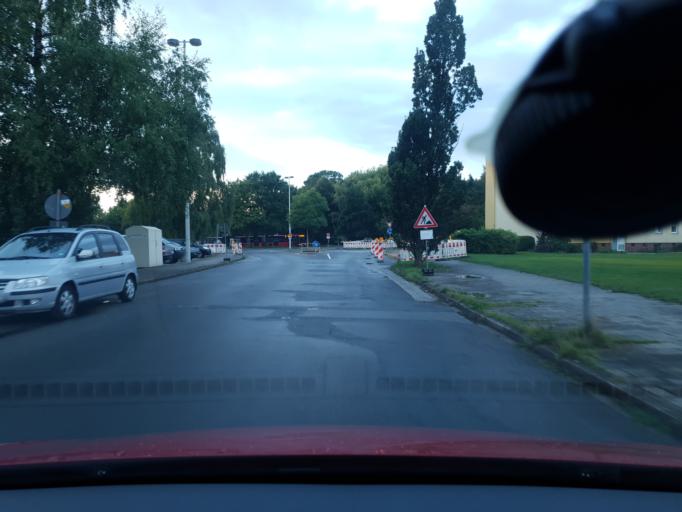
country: DE
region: Schleswig-Holstein
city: Kronshagen
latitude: 54.3612
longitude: 10.0774
